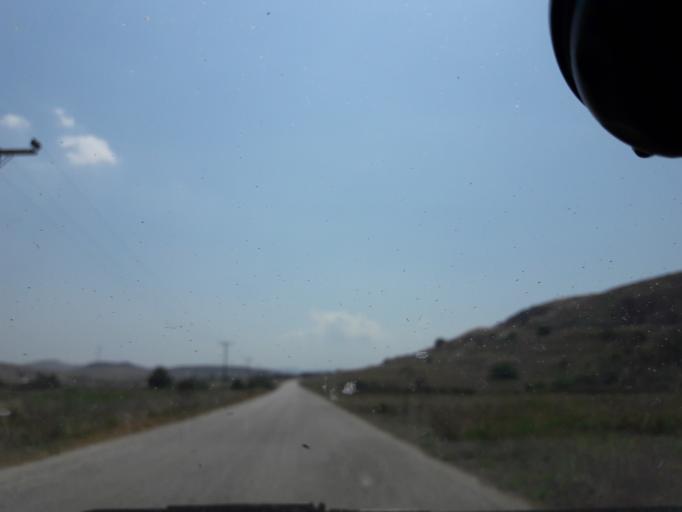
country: GR
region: North Aegean
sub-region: Nomos Lesvou
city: Myrina
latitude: 39.9119
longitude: 25.3156
